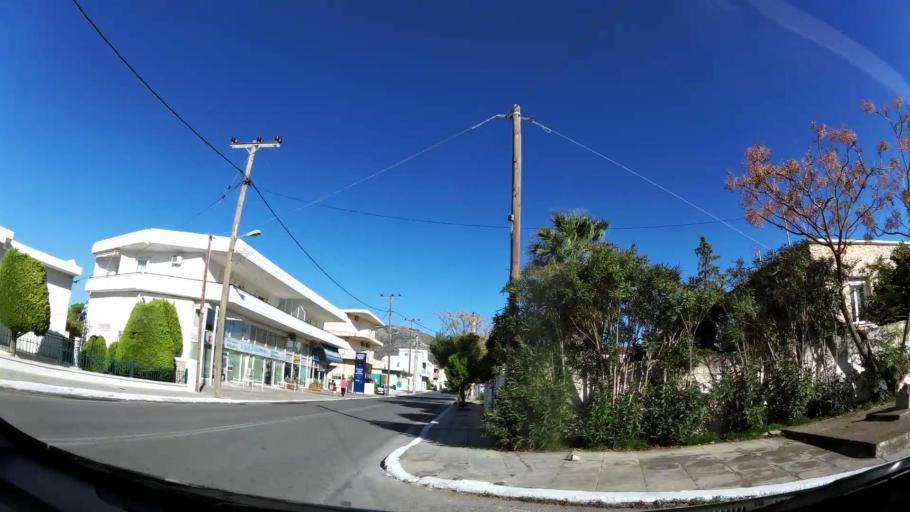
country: GR
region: Attica
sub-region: Nomarchia Anatolikis Attikis
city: Kalyvia Thorikou
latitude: 37.8388
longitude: 23.9247
